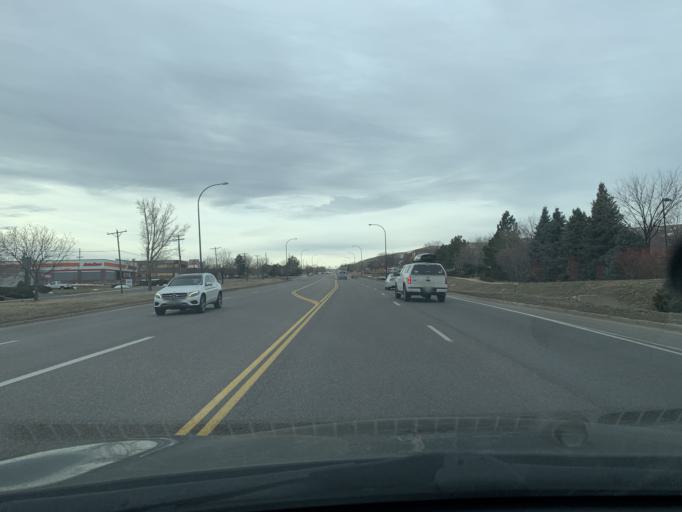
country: US
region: Colorado
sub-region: Jefferson County
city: West Pleasant View
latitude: 39.7068
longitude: -105.1361
